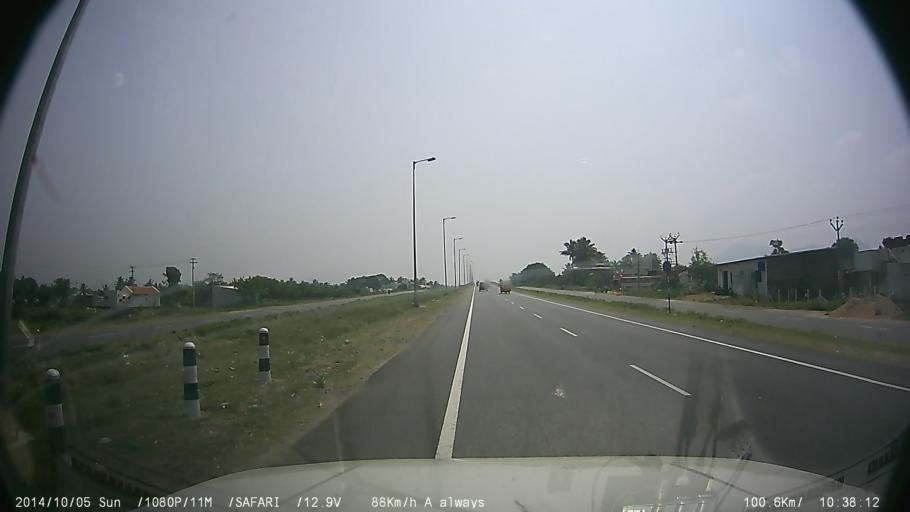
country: IN
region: Tamil Nadu
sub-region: Salem
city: Salem
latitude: 11.6640
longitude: 78.2381
